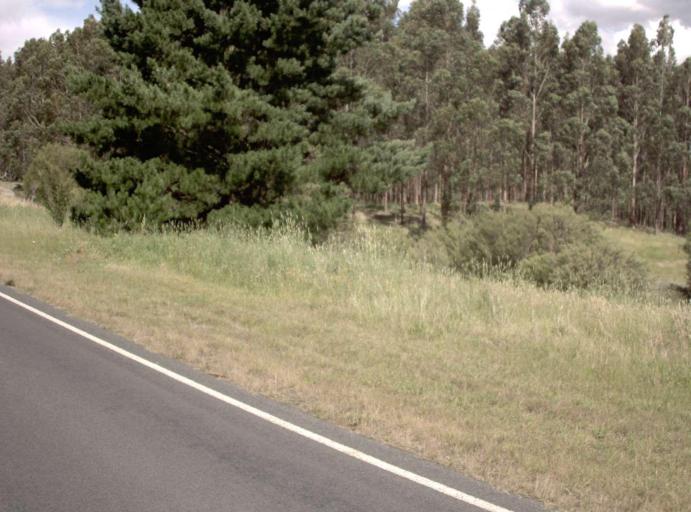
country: AU
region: Victoria
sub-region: Latrobe
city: Morwell
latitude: -38.1579
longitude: 146.4220
